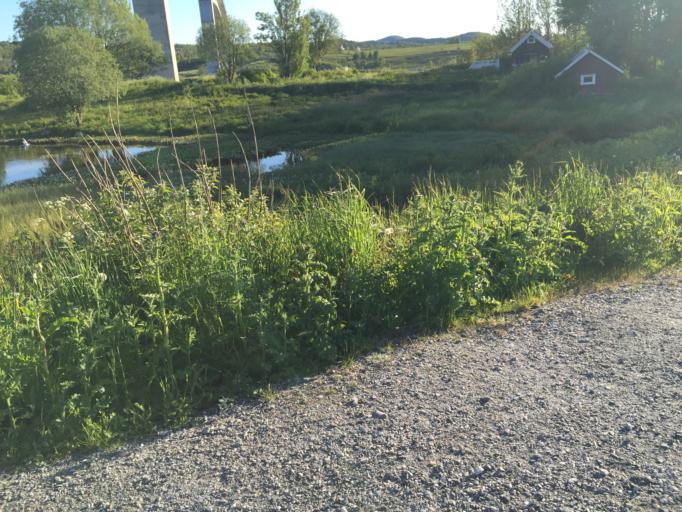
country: NO
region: Nordland
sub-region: Bodo
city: Loding
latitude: 67.2325
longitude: 14.6171
